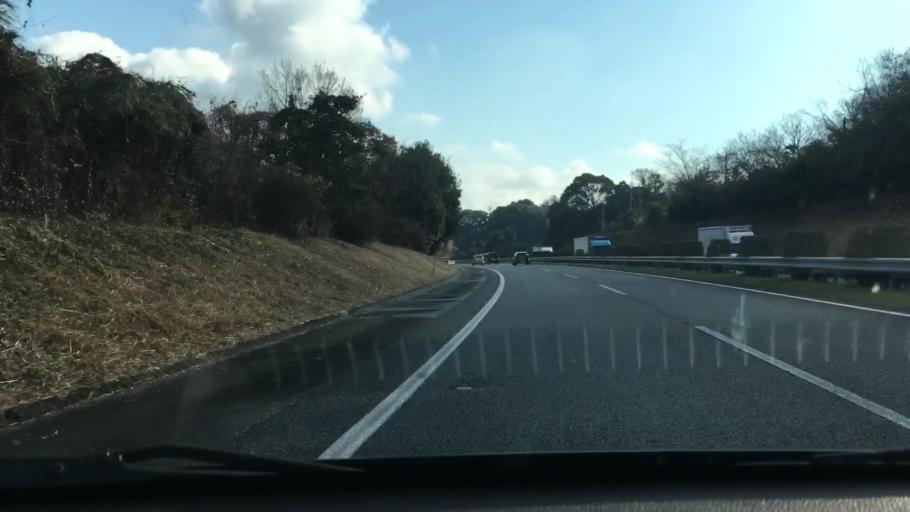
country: JP
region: Kumamoto
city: Matsubase
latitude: 32.6410
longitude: 130.7071
